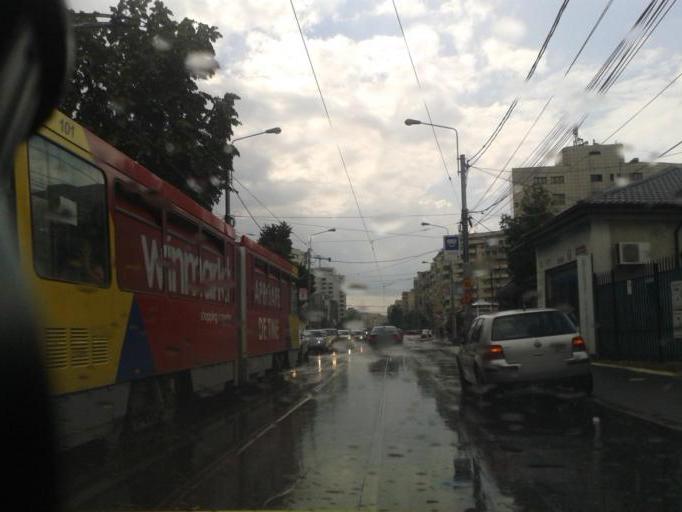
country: RO
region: Prahova
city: Ploiesti
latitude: 44.9453
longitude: 26.0210
